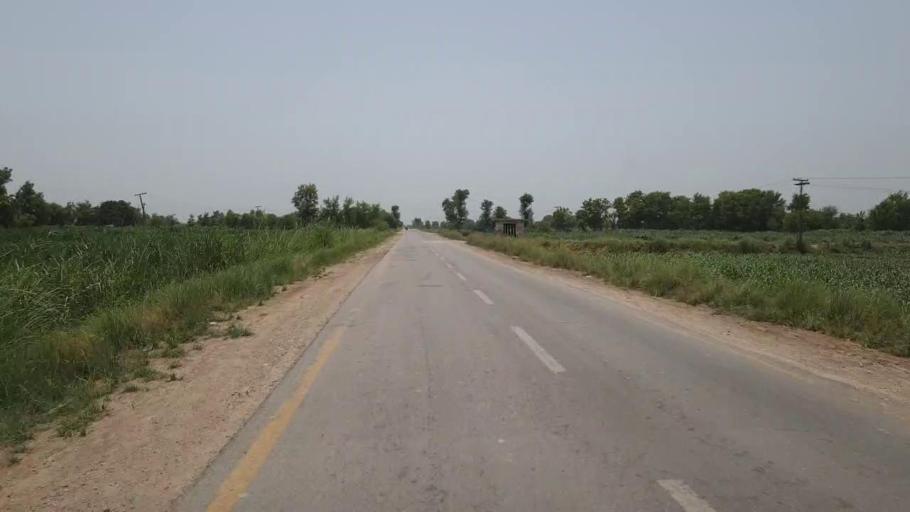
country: PK
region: Sindh
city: Moro
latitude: 26.5991
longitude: 68.0979
